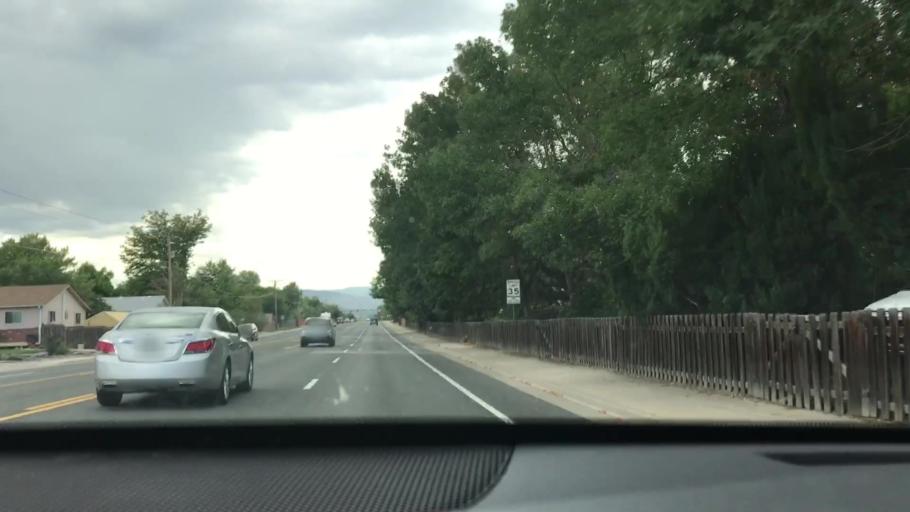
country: US
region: Colorado
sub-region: Larimer County
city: Loveland
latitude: 40.3785
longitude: -105.1100
